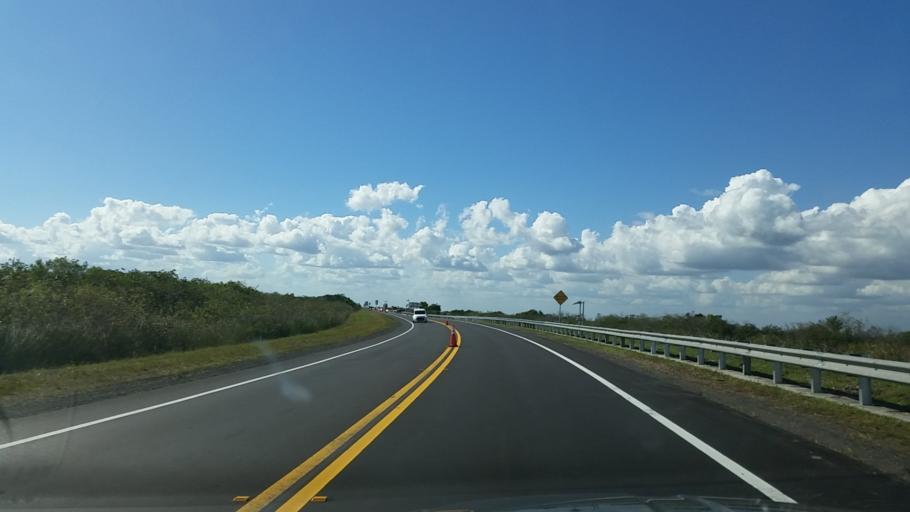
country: US
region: Florida
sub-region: Miami-Dade County
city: Kendall West
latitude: 25.7616
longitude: -80.6753
